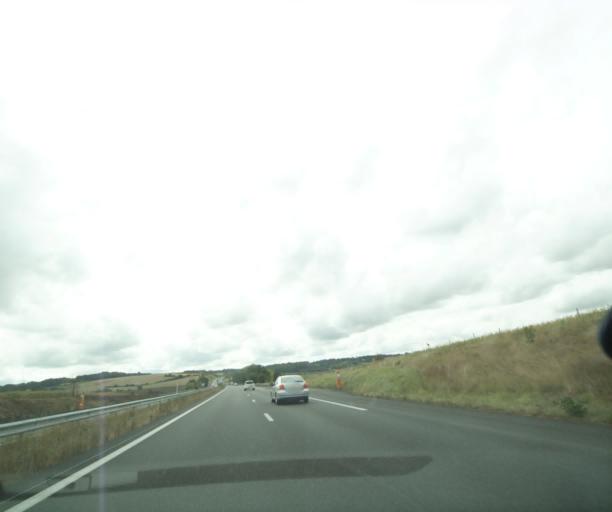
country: FR
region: Poitou-Charentes
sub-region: Departement de la Charente-Maritime
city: Mirambeau
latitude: 45.4236
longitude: -0.6047
